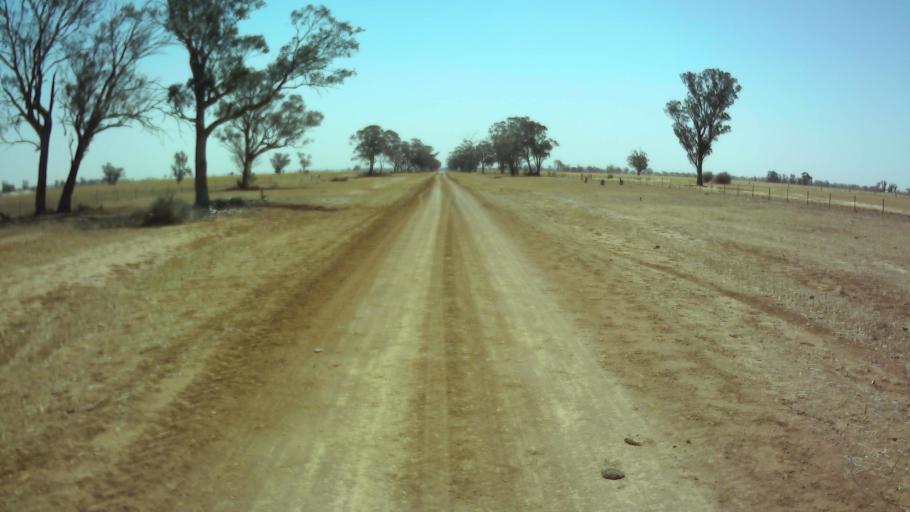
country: AU
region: New South Wales
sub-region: Weddin
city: Grenfell
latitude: -34.0102
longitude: 147.8908
